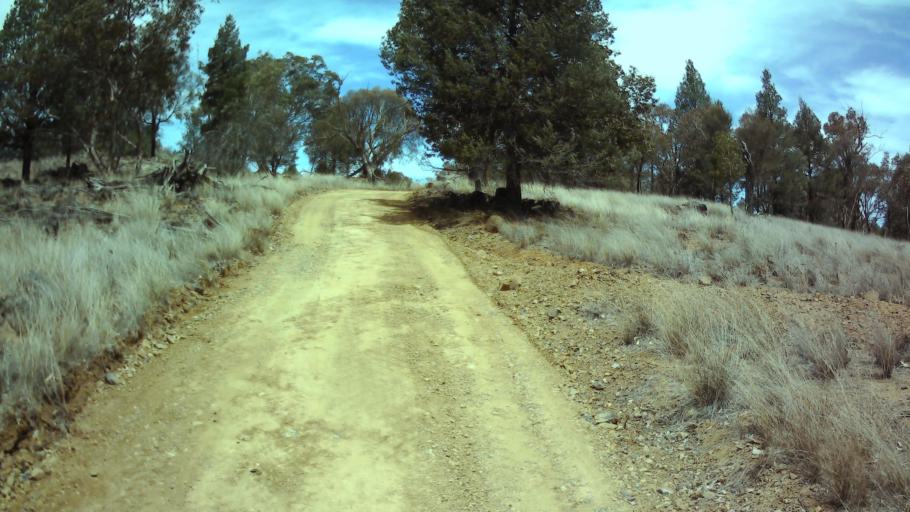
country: AU
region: New South Wales
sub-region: Weddin
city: Grenfell
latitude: -33.7872
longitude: 148.1556
